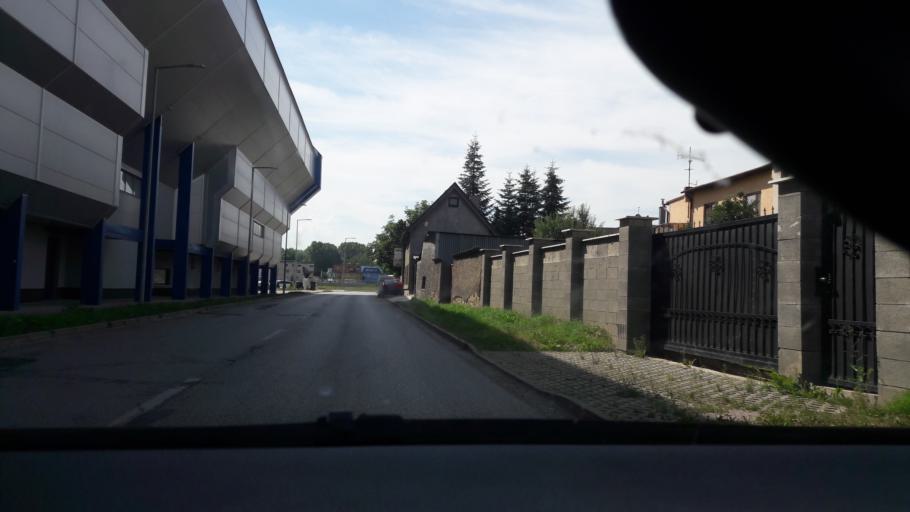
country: SK
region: Presovsky
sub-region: Okres Presov
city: Kezmarok
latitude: 49.1362
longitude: 20.4330
